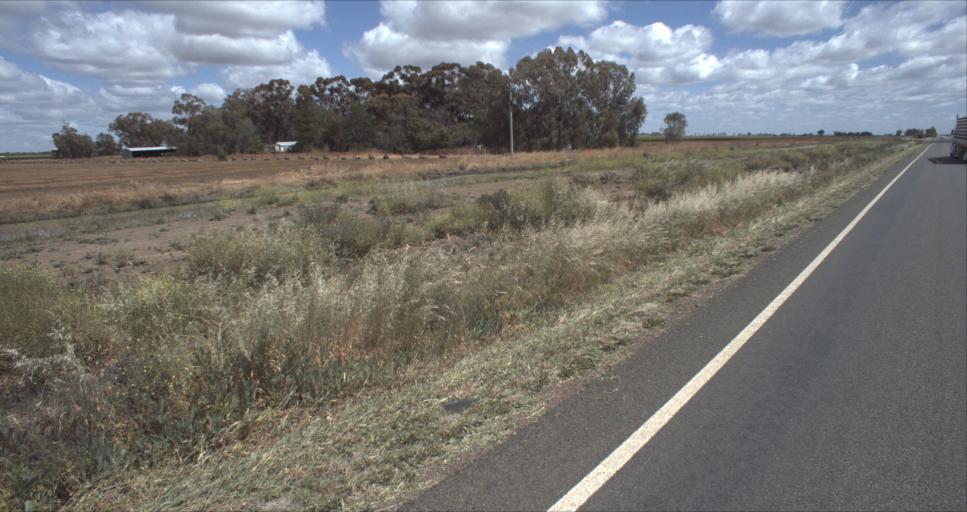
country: AU
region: New South Wales
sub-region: Murrumbidgee Shire
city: Darlington Point
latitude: -34.4842
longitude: 146.1578
